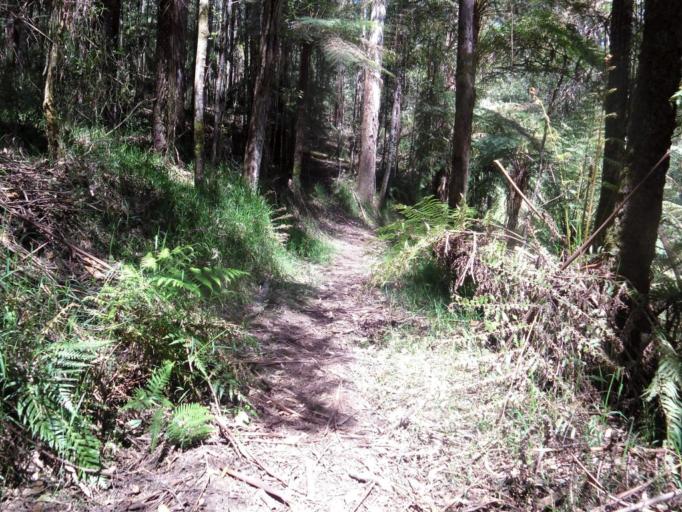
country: AU
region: Victoria
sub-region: Yarra Ranges
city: Millgrove
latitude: -37.8638
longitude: 145.7629
